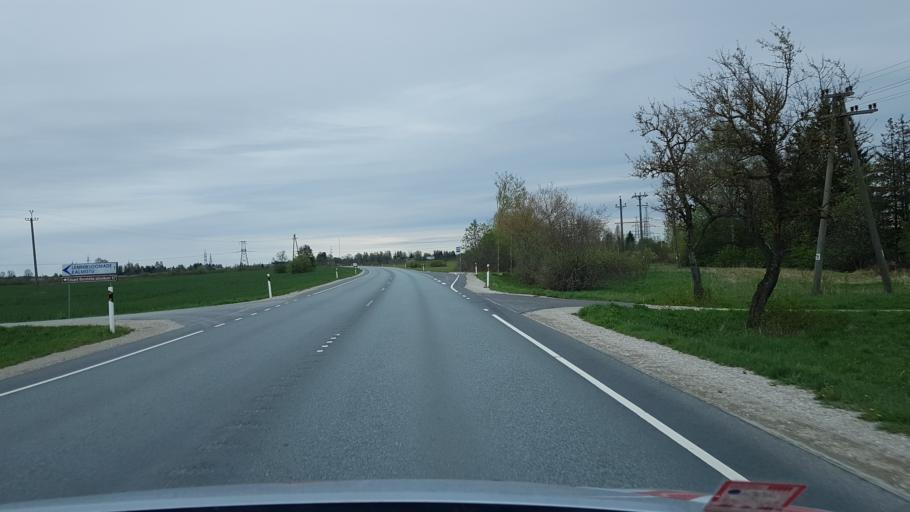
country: EE
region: Laeaene-Virumaa
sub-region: Rakvere linn
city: Rakvere
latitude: 59.3521
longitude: 26.3120
